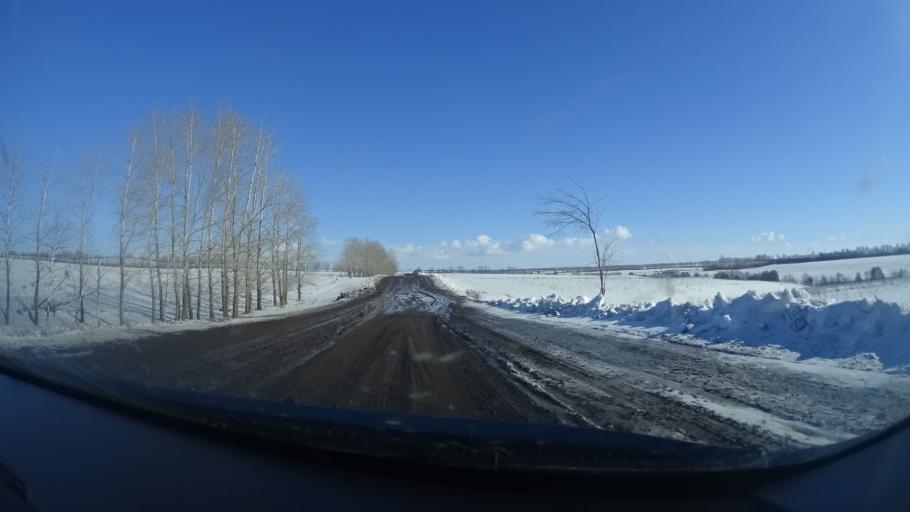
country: RU
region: Bashkortostan
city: Chishmy
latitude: 54.6009
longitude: 55.2254
